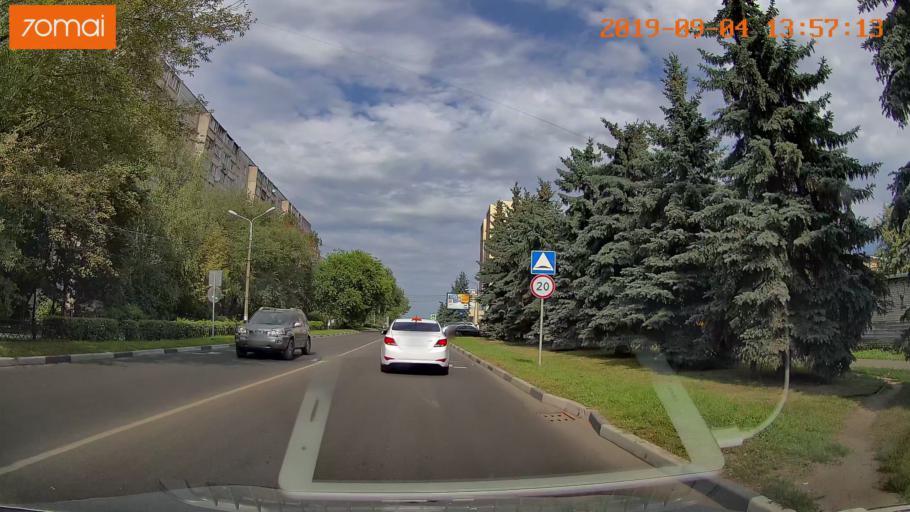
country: RU
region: Moskovskaya
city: Bykovo
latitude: 55.6075
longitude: 38.0757
